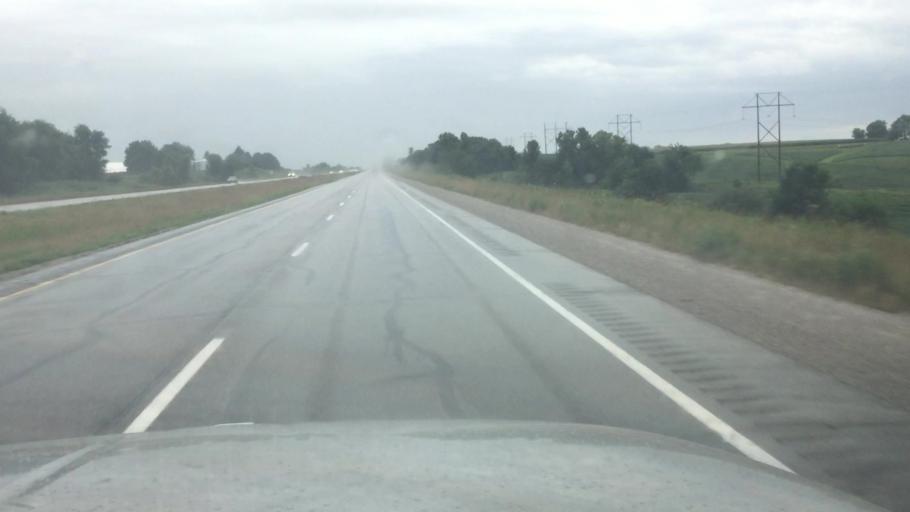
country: US
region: Iowa
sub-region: Johnson County
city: Lone Tree
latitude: 41.4189
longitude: -91.5511
